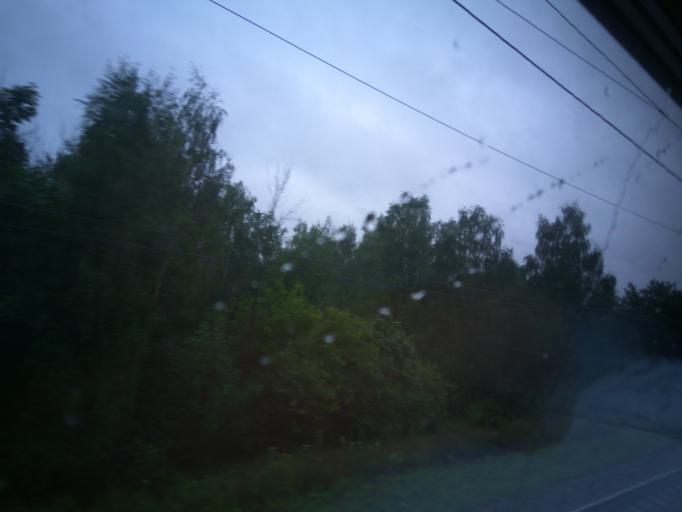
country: RU
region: Moskovskaya
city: Stupino
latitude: 54.8802
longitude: 38.1069
